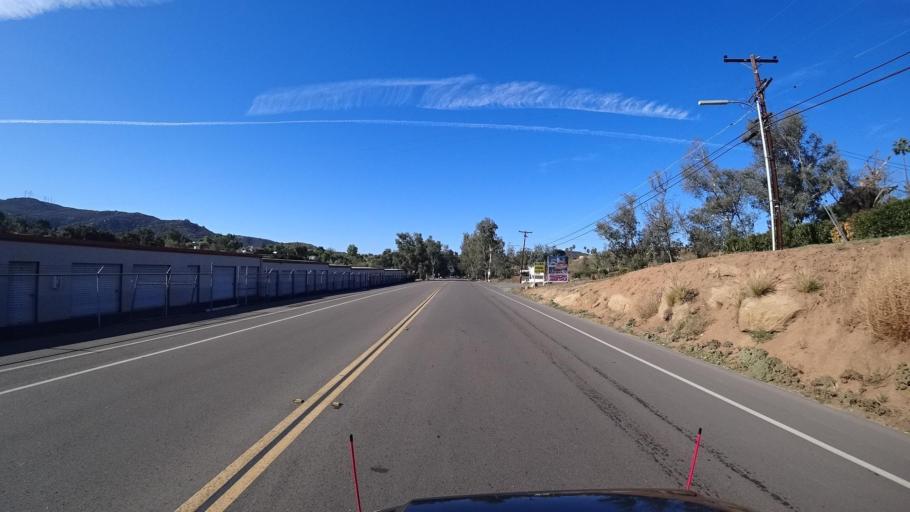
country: US
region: California
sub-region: San Diego County
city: Lakeside
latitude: 32.8393
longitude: -116.8953
